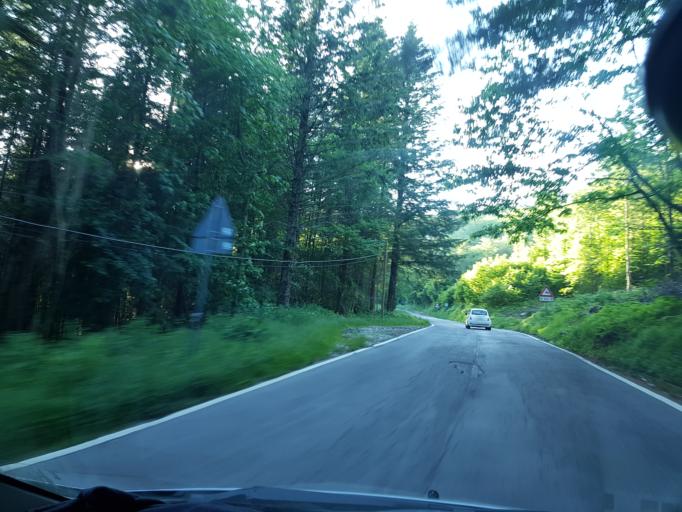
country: IT
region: Tuscany
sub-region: Provincia di Lucca
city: Minucciano
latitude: 44.1633
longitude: 10.2175
